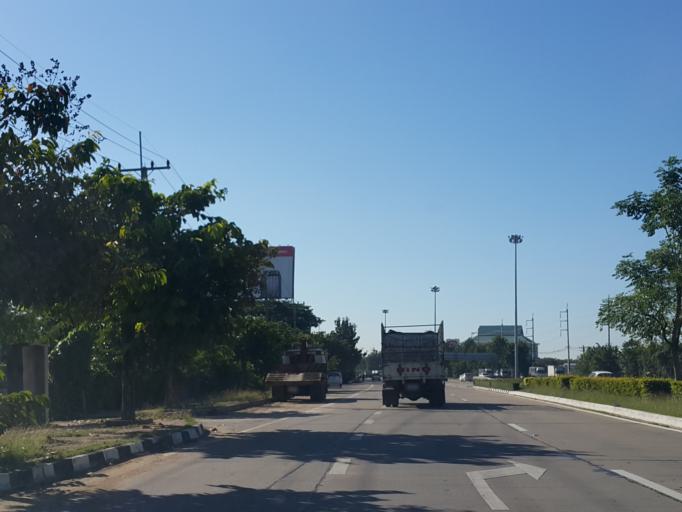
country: TH
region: Chiang Mai
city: Saraphi
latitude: 18.7614
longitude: 99.0301
